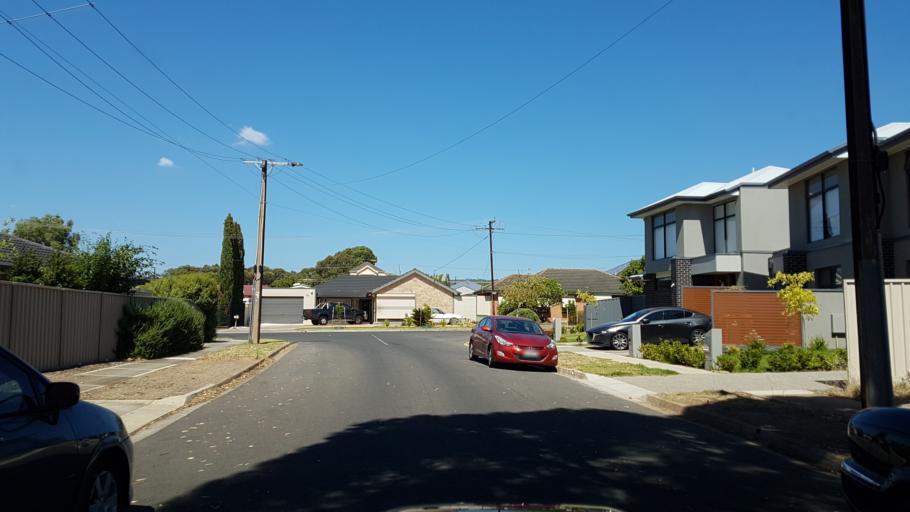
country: AU
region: South Australia
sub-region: Marion
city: Clovelly Park
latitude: -35.0043
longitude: 138.5641
